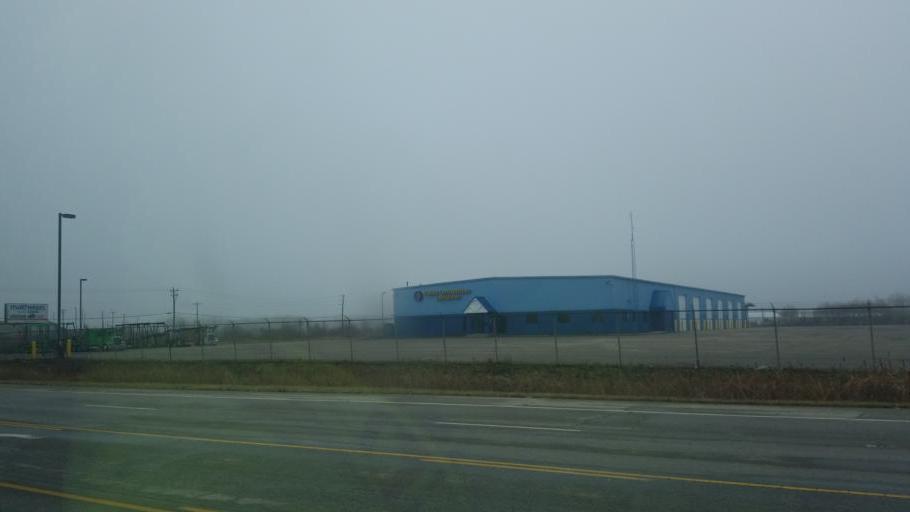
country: US
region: Ohio
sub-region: Champaign County
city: North Lewisburg
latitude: 40.2765
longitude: -83.5178
